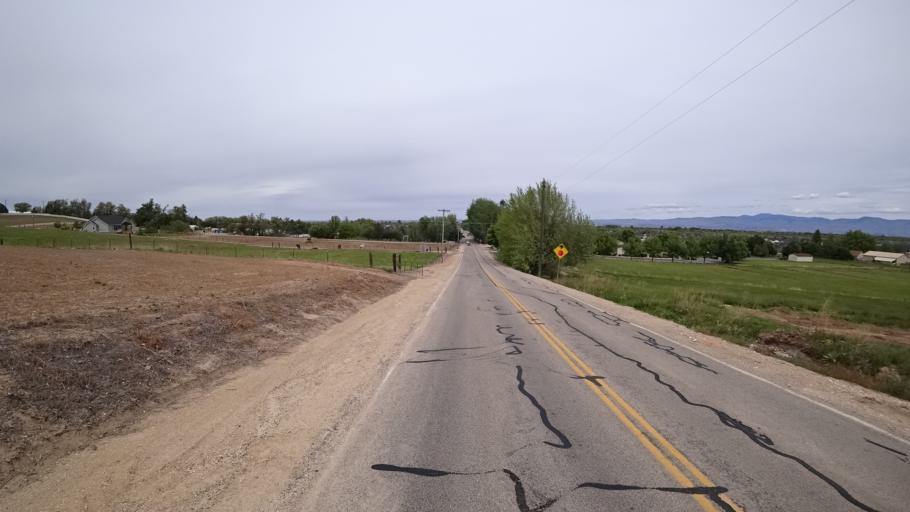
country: US
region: Idaho
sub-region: Ada County
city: Meridian
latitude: 43.5592
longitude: -116.3745
